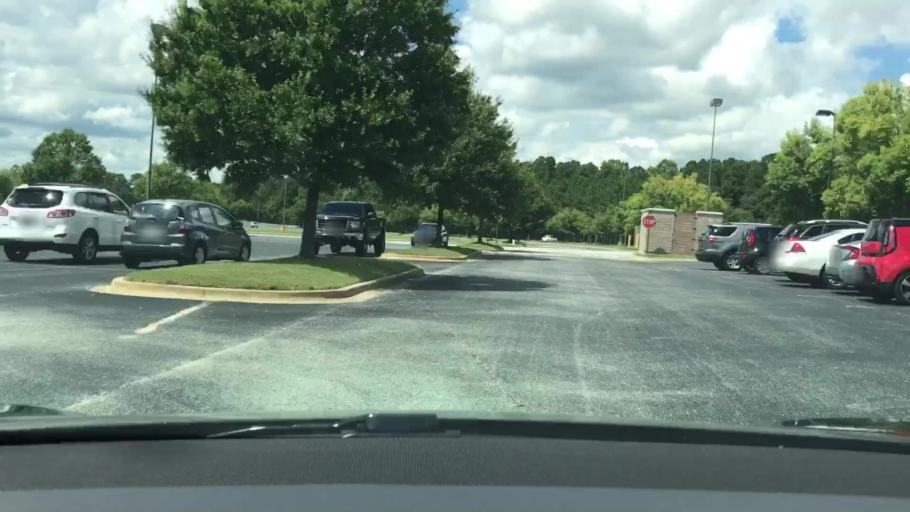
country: US
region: Alabama
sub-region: Lee County
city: Auburn
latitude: 32.6274
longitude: -85.4449
